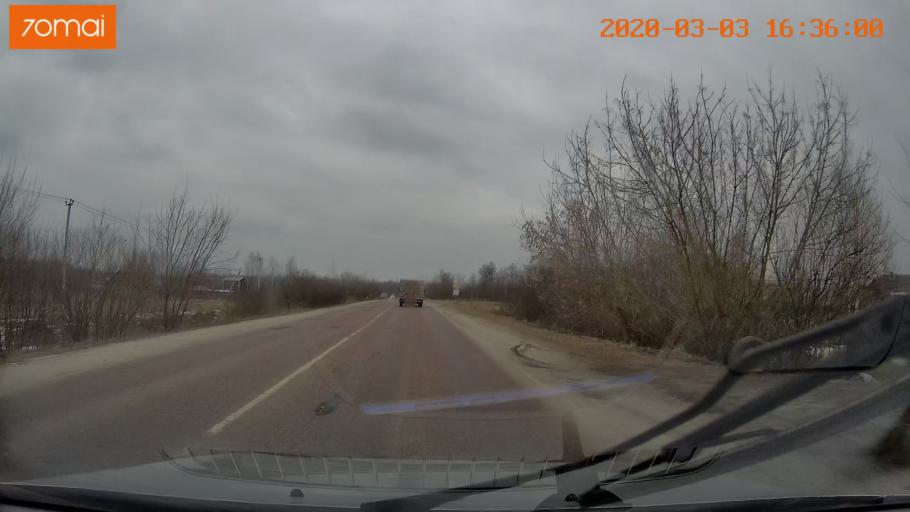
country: RU
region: Moskovskaya
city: Lopatinskiy
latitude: 55.4012
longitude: 38.7672
